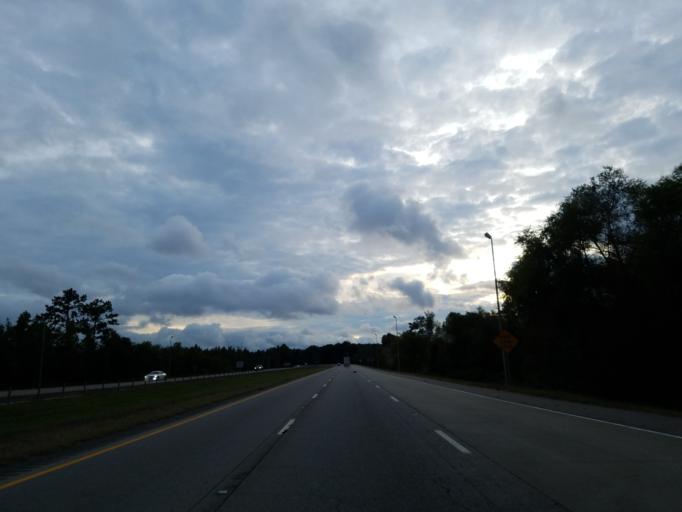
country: US
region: Alabama
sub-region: Sumter County
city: York
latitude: 32.4342
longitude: -88.4430
